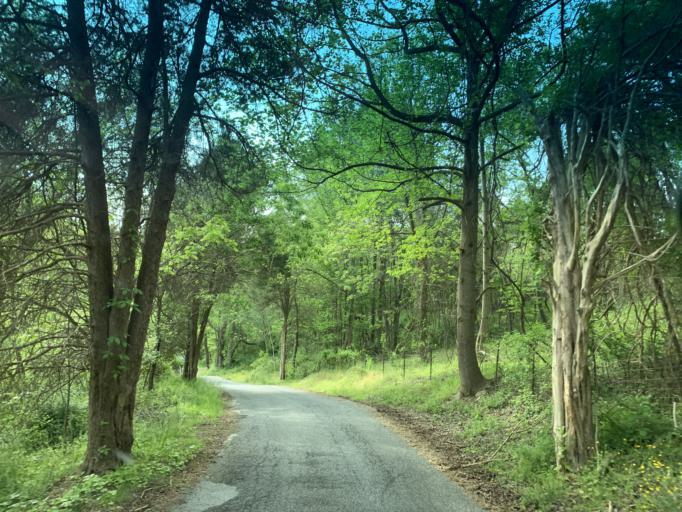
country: US
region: Maryland
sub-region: Baltimore County
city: Perry Hall
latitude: 39.4271
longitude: -76.4882
